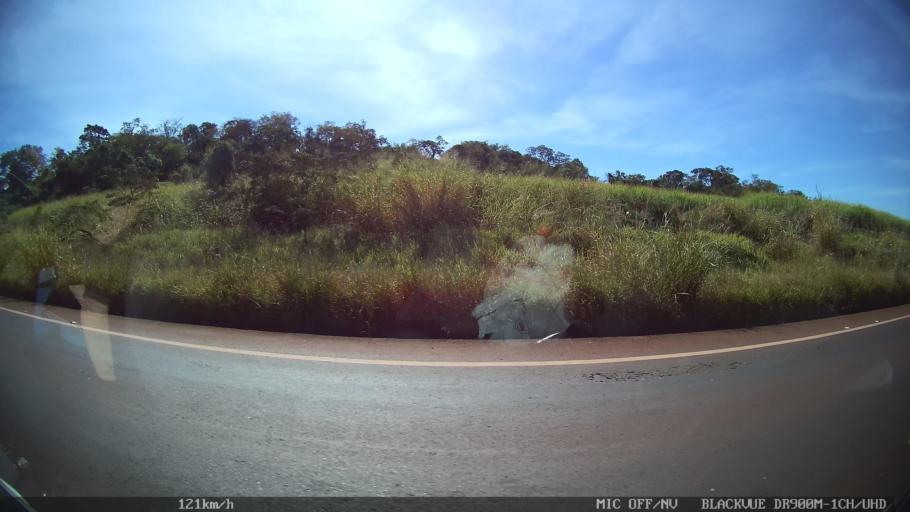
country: BR
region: Sao Paulo
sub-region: Sao Joaquim Da Barra
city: Sao Joaquim da Barra
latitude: -20.5398
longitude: -47.8132
